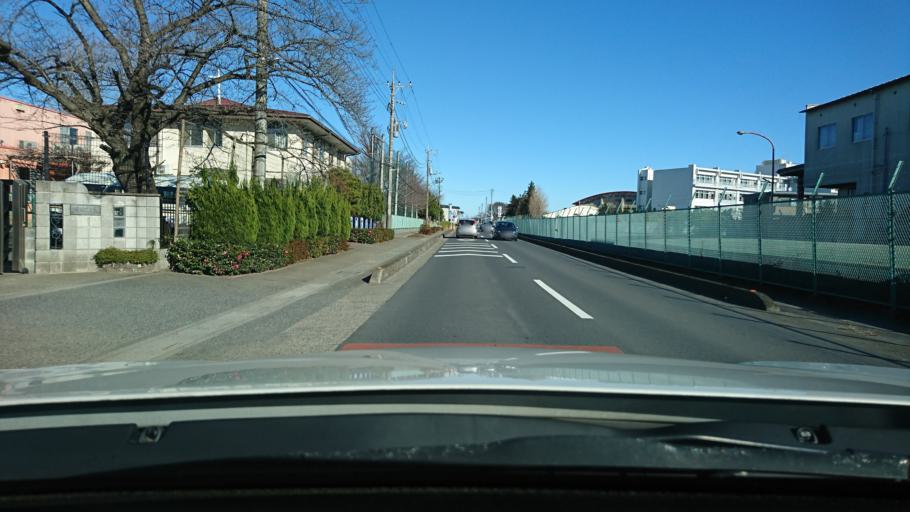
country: JP
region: Saitama
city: Kamifukuoka
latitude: 35.8867
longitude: 139.5156
